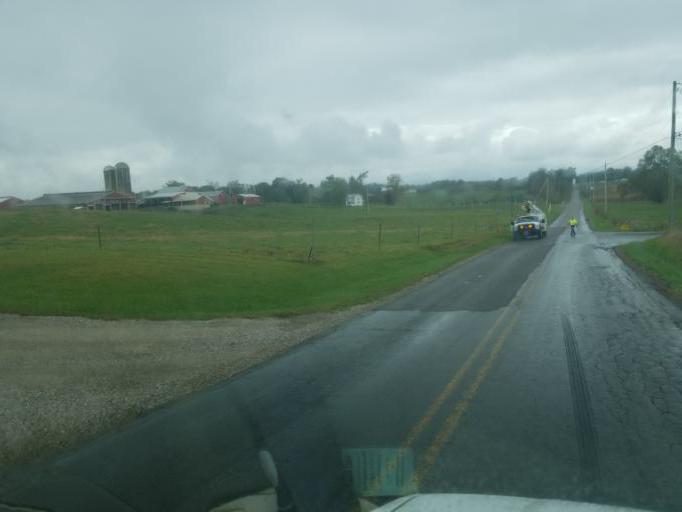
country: US
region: Ohio
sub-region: Wayne County
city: Shreve
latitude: 40.6682
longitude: -82.0245
